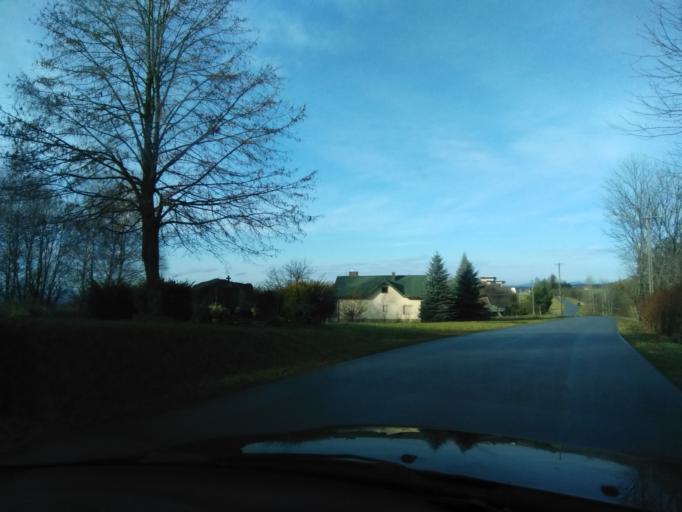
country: PL
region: Subcarpathian Voivodeship
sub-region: Powiat krosnienski
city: Korczyna
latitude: 49.7300
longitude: 21.7894
